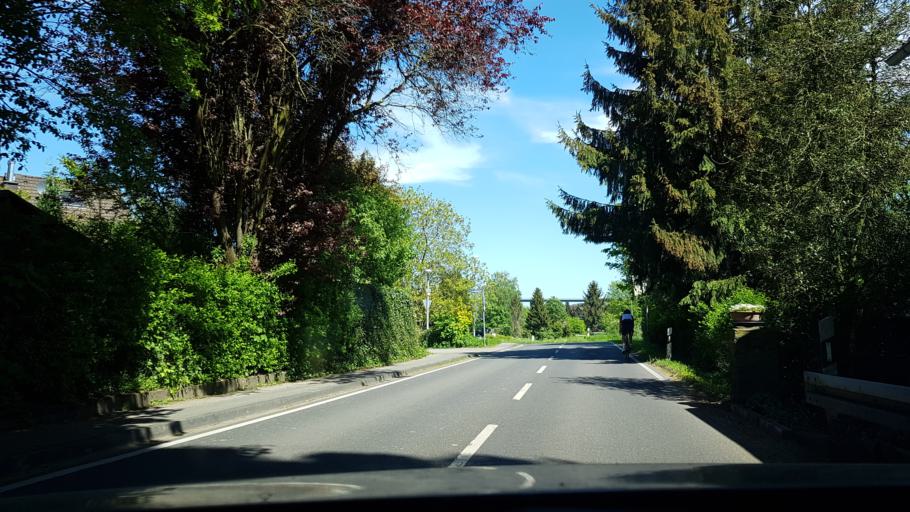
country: DE
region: North Rhine-Westphalia
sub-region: Regierungsbezirk Dusseldorf
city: Muelheim (Ruhr)
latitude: 51.3694
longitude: 6.9039
